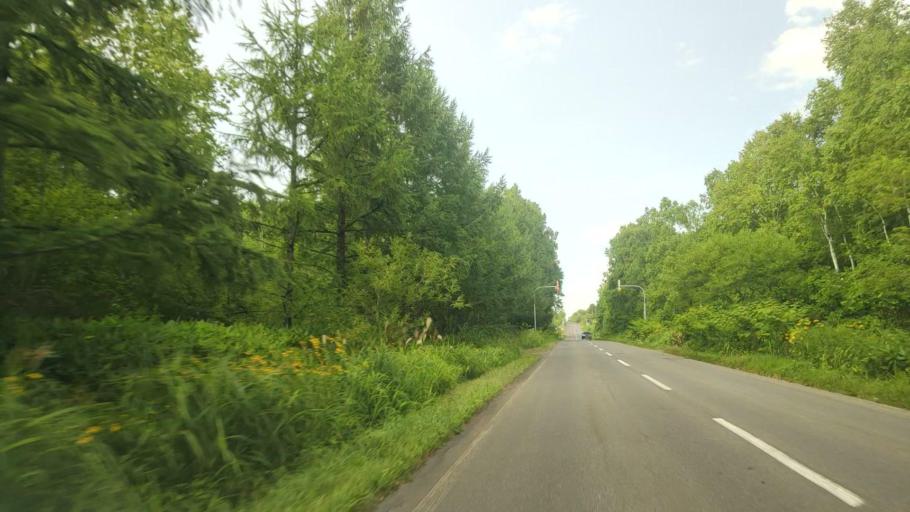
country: JP
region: Hokkaido
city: Nayoro
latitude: 44.2437
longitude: 142.4157
